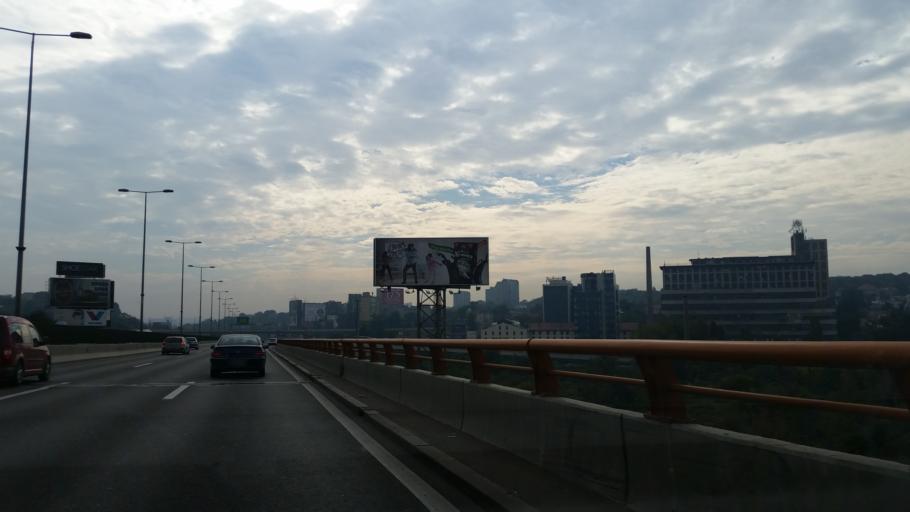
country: RS
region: Central Serbia
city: Belgrade
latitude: 44.8007
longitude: 20.4447
